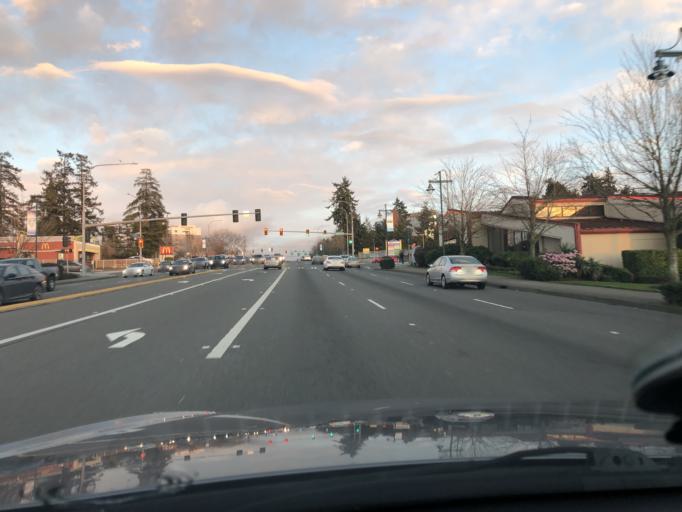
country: US
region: Washington
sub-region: King County
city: Federal Way
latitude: 47.3150
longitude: -122.3047
